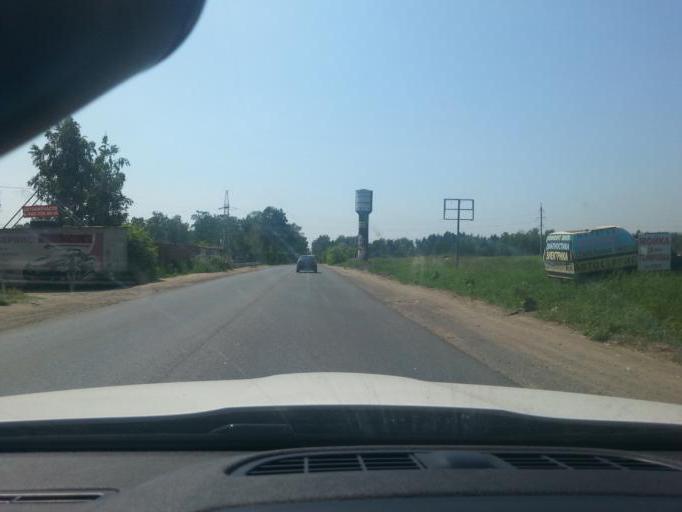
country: RU
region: Moskovskaya
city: Zheleznodorozhnyy
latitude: 55.7227
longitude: 37.9748
